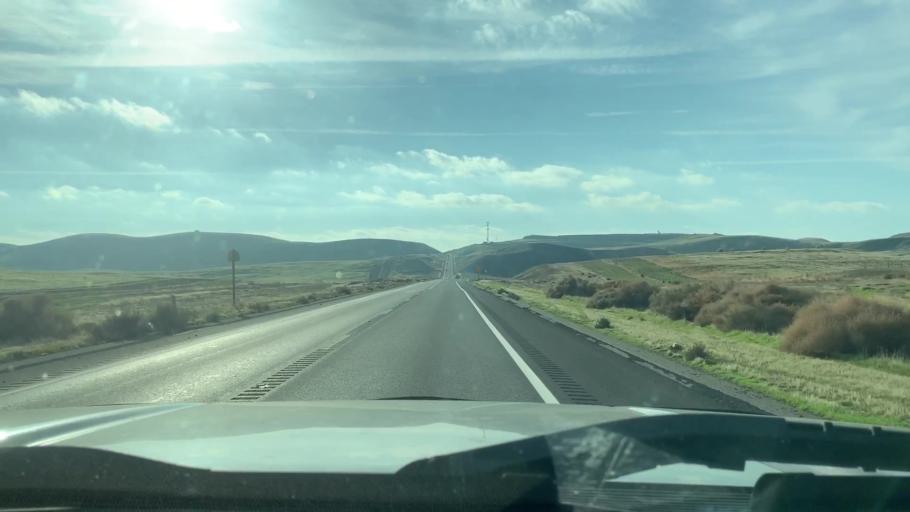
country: US
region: California
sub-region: Kings County
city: Kettleman City
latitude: 35.9560
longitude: -119.9897
